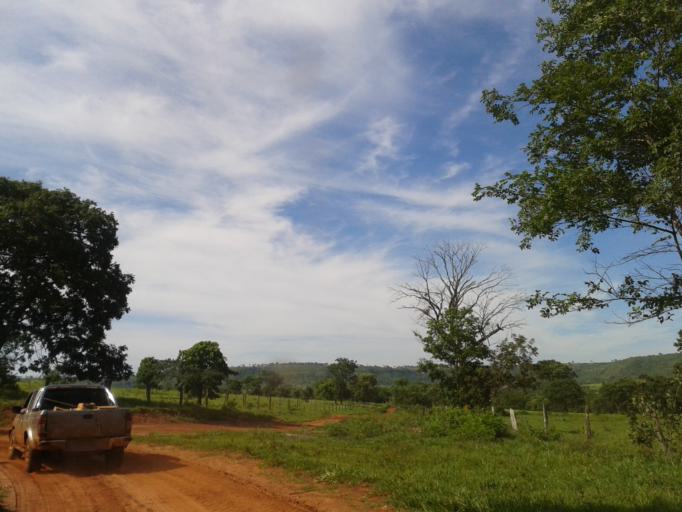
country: BR
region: Minas Gerais
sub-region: Santa Vitoria
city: Santa Vitoria
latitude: -19.0799
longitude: -50.0161
